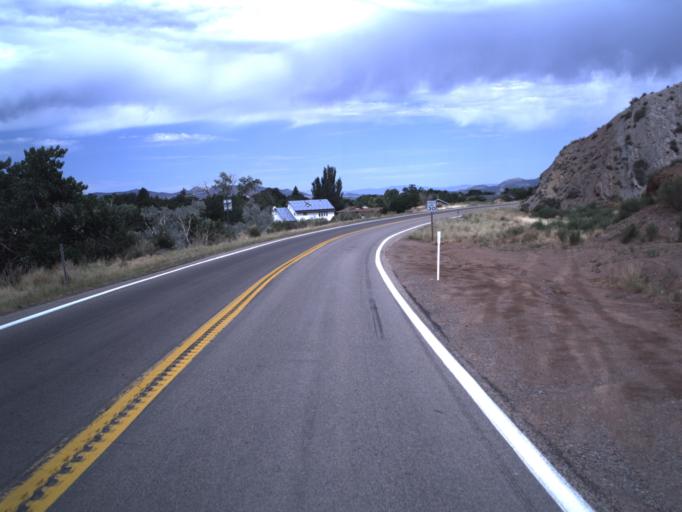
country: US
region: Utah
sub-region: Iron County
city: Cedar City
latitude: 37.6749
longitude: -113.0489
